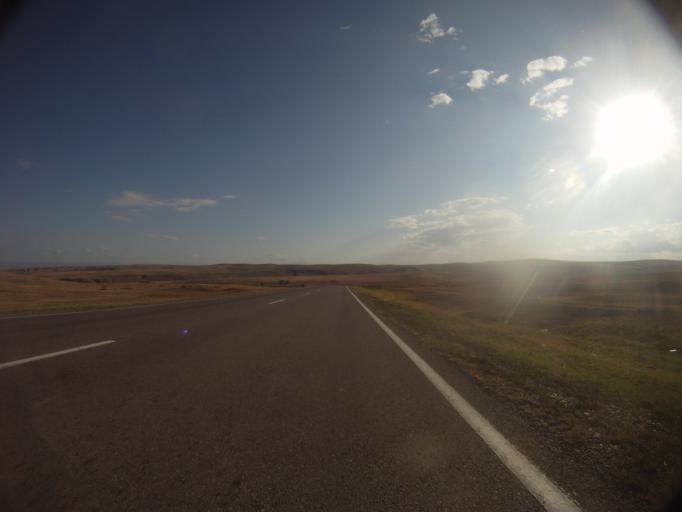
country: GE
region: Kvemo Kartli
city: Rust'avi
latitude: 41.5293
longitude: 44.9393
